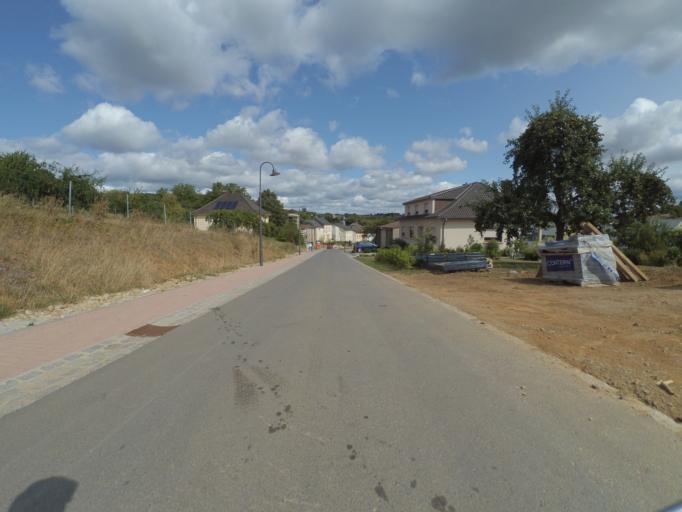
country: LU
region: Grevenmacher
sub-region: Canton de Remich
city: Lenningen
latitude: 49.5832
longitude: 6.3574
